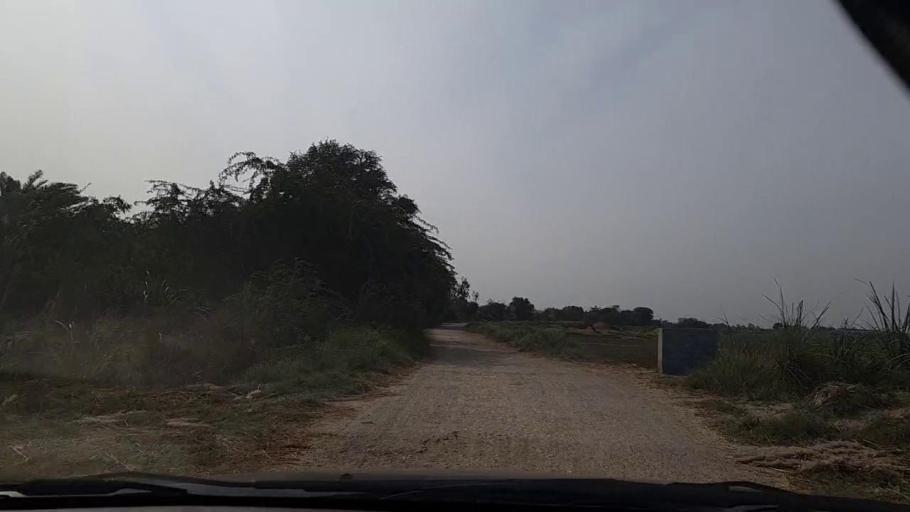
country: PK
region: Sindh
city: Thatta
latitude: 24.5720
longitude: 67.8770
